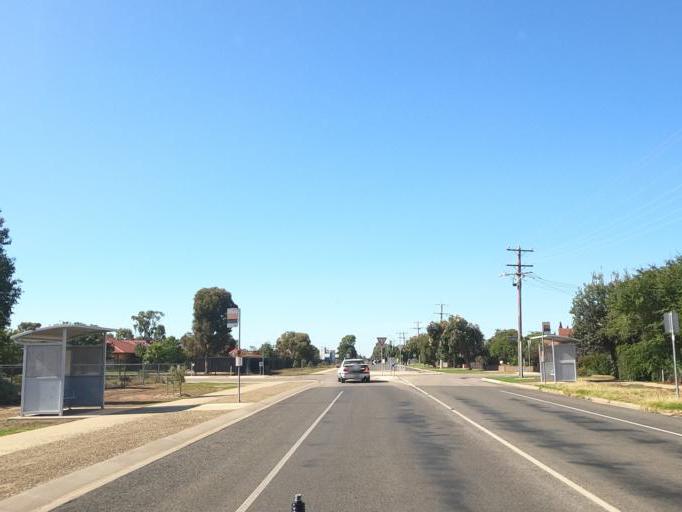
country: AU
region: Victoria
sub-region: Moira
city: Yarrawonga
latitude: -36.0125
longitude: 146.0132
